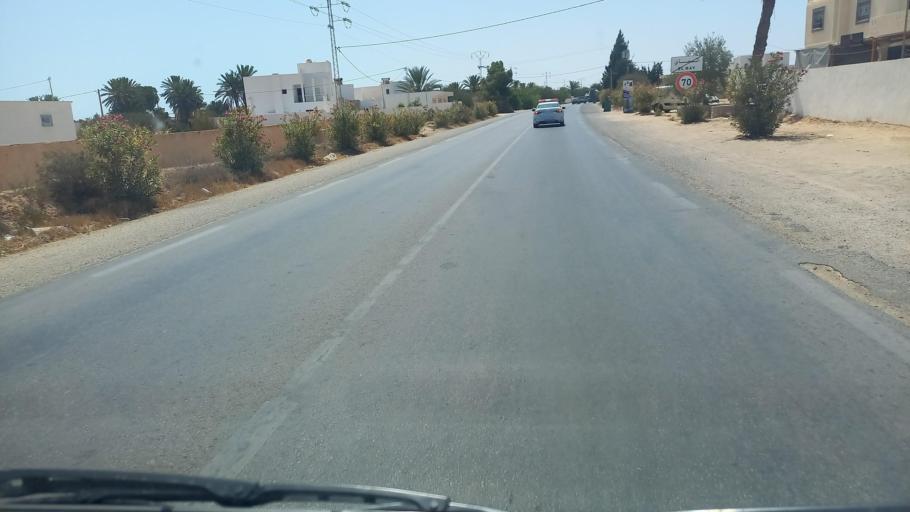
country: TN
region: Madanin
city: Houmt Souk
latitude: 33.7956
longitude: 10.8862
